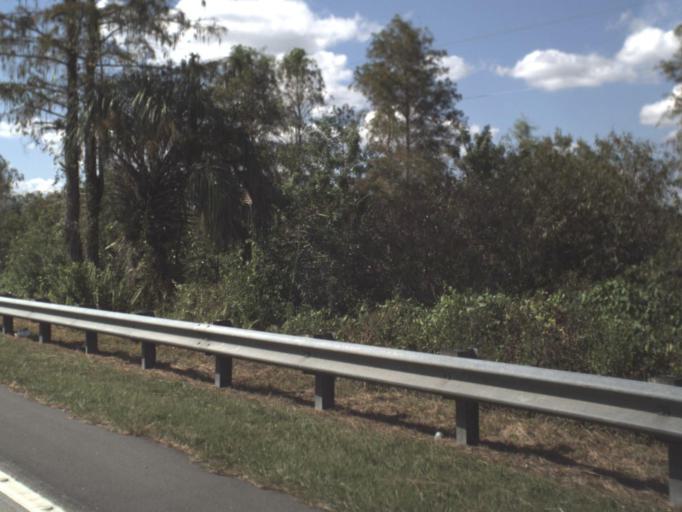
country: US
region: Florida
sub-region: Miami-Dade County
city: Kendall West
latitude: 25.8604
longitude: -81.0682
